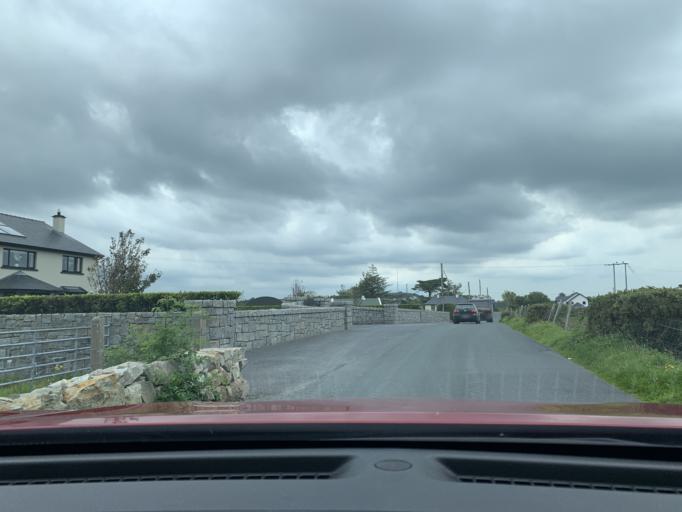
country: IE
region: Connaught
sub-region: County Galway
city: Bearna
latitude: 53.2774
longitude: -9.1180
